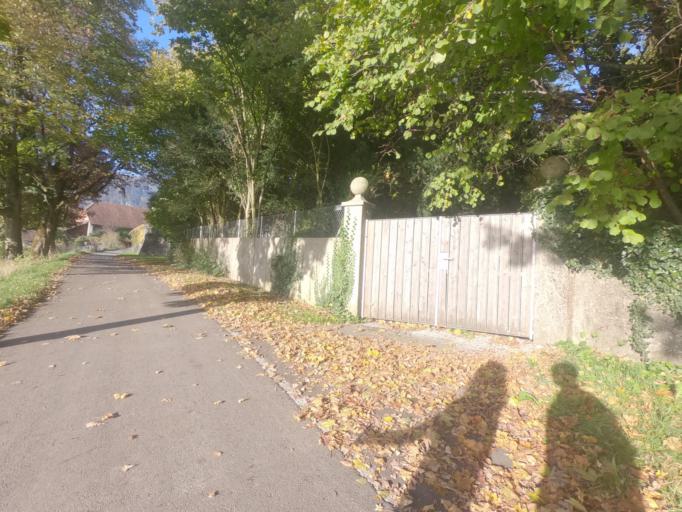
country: CH
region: Solothurn
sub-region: Bezirk Lebern
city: Langendorf
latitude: 47.2192
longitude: 7.5285
